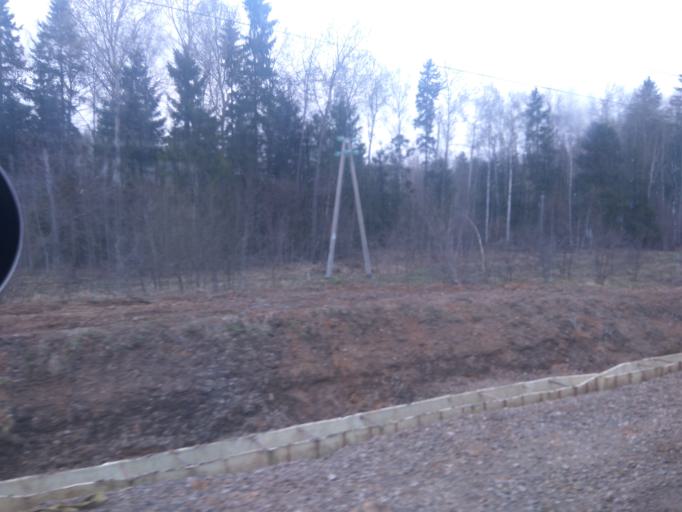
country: RU
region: Moskovskaya
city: Skoropuskovskiy
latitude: 56.3510
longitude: 38.1472
